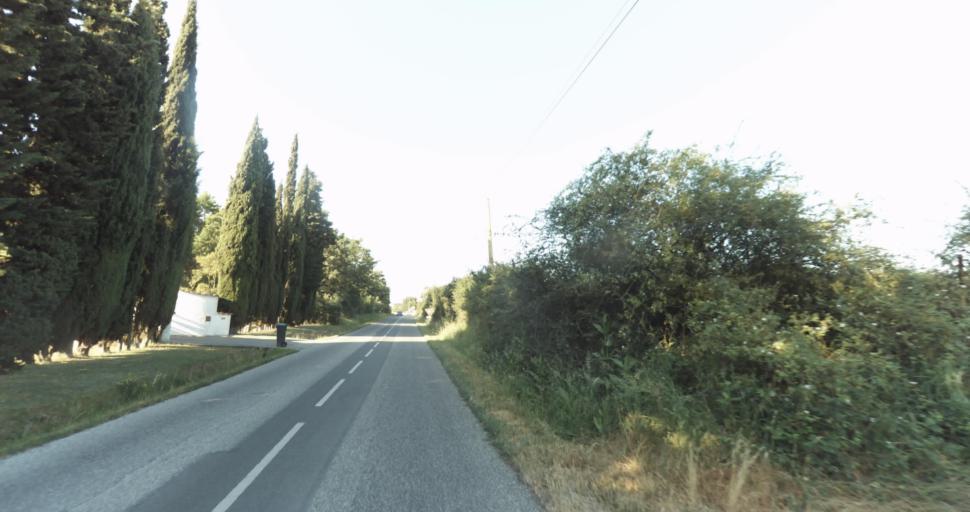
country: FR
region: Midi-Pyrenees
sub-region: Departement de la Haute-Garonne
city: Leguevin
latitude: 43.5709
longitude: 1.2344
